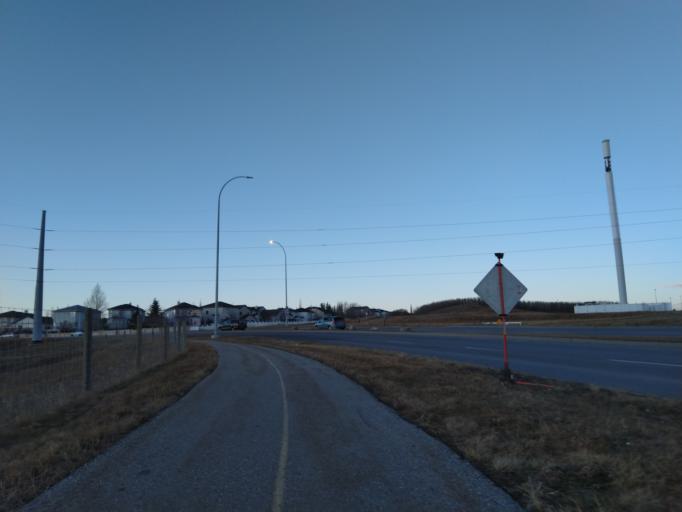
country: CA
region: Alberta
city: Calgary
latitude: 51.1243
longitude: -114.2334
